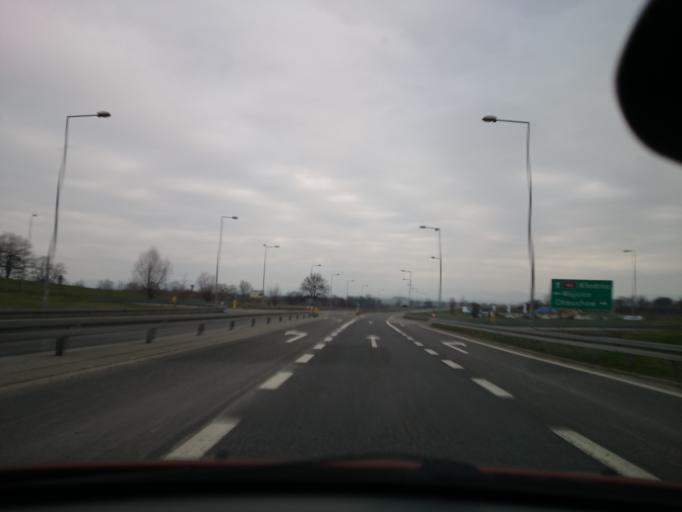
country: PL
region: Opole Voivodeship
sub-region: Powiat nyski
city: Otmuchow
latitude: 50.4617
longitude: 17.1962
